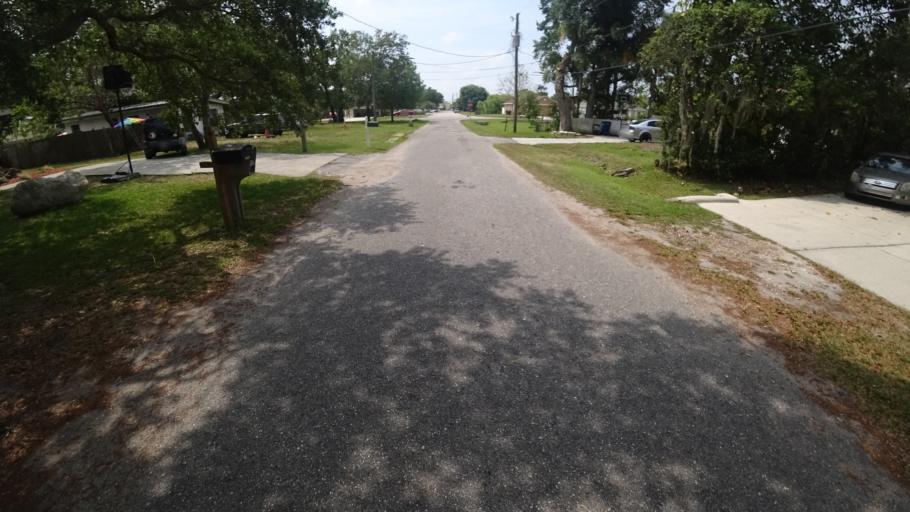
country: US
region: Florida
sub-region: Manatee County
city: Samoset
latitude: 27.4683
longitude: -82.5449
